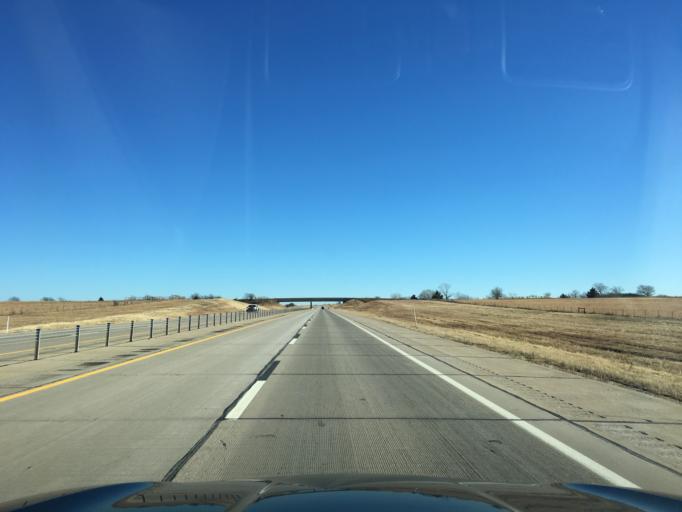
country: US
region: Oklahoma
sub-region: Noble County
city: Perry
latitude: 36.3930
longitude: -97.1981
